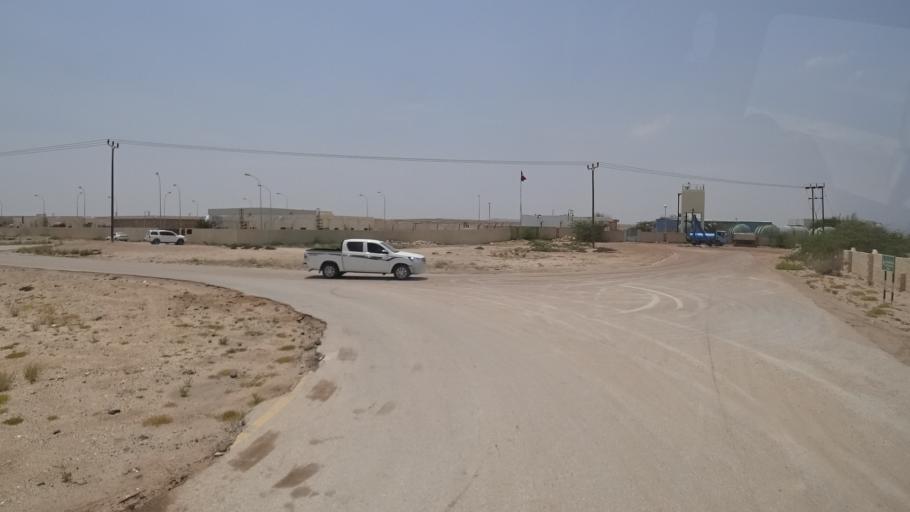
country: OM
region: Ash Sharqiyah
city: Sur
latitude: 22.5301
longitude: 59.7643
